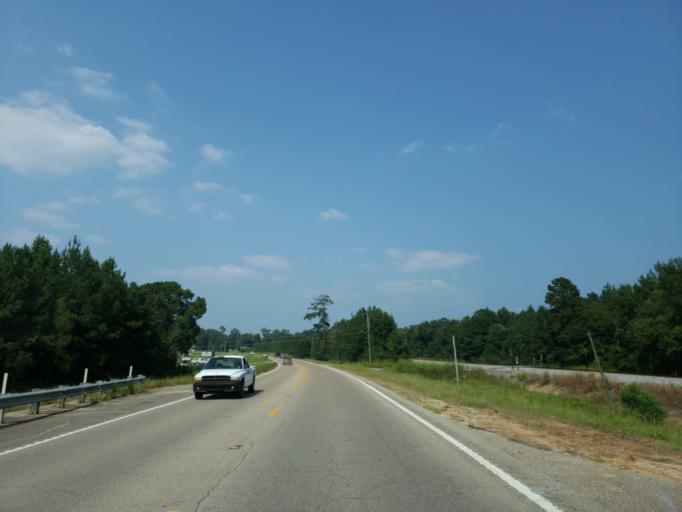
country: US
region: Mississippi
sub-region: Jones County
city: Ellisville
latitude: 31.6224
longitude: -89.1832
